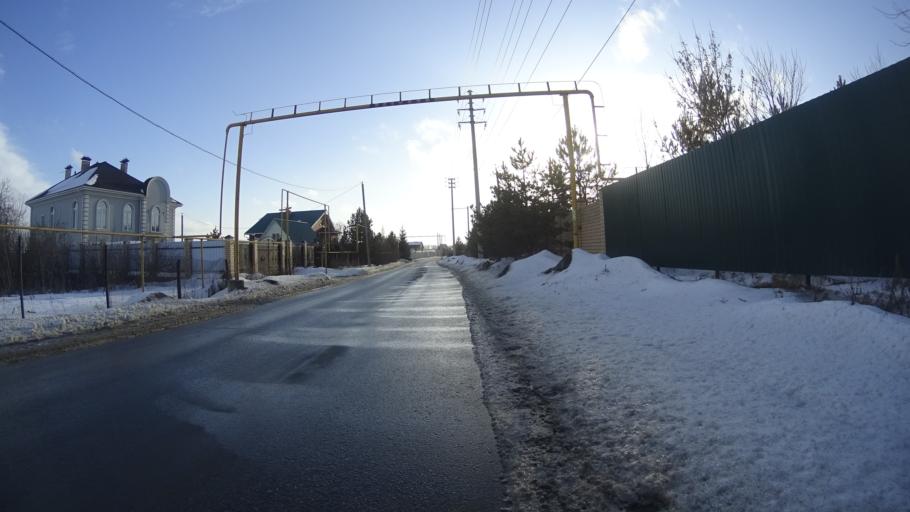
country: RU
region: Chelyabinsk
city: Sargazy
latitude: 55.1118
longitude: 61.2798
